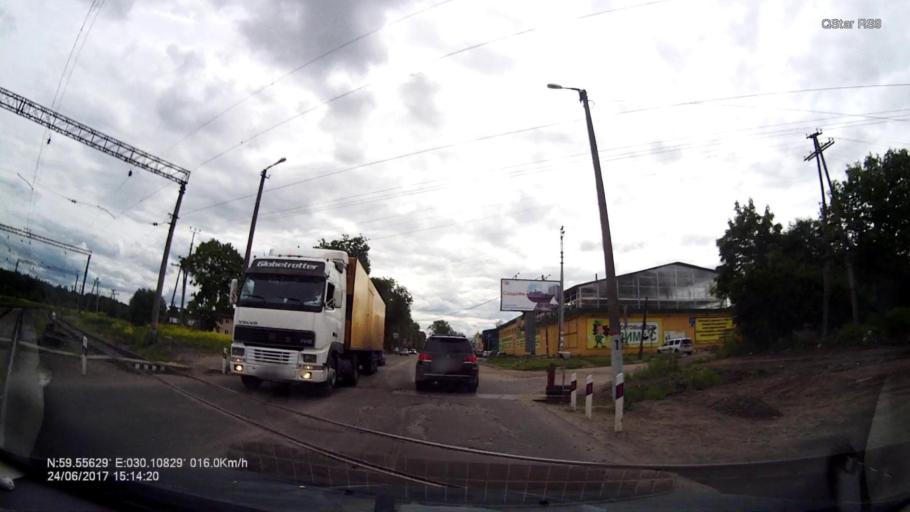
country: RU
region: Leningrad
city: Gatchina
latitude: 59.5562
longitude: 30.1082
